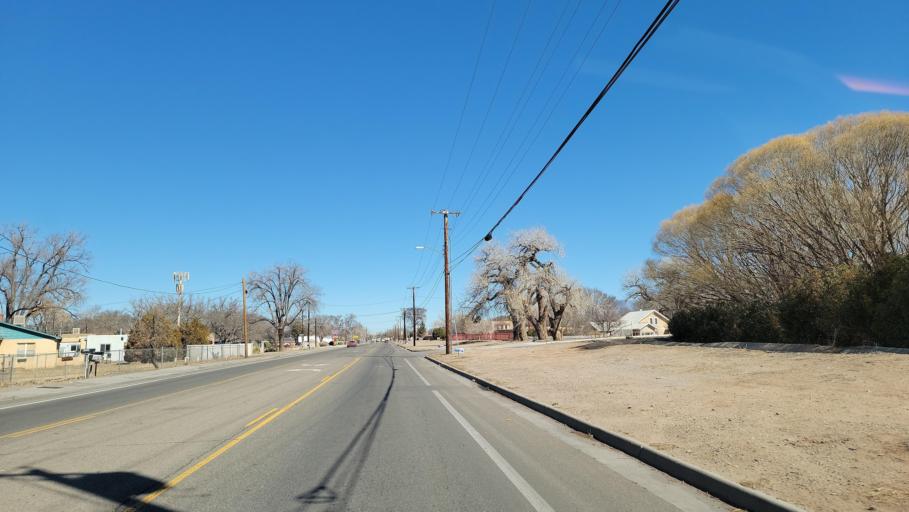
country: US
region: New Mexico
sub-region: Bernalillo County
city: South Valley
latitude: 35.0128
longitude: -106.6865
